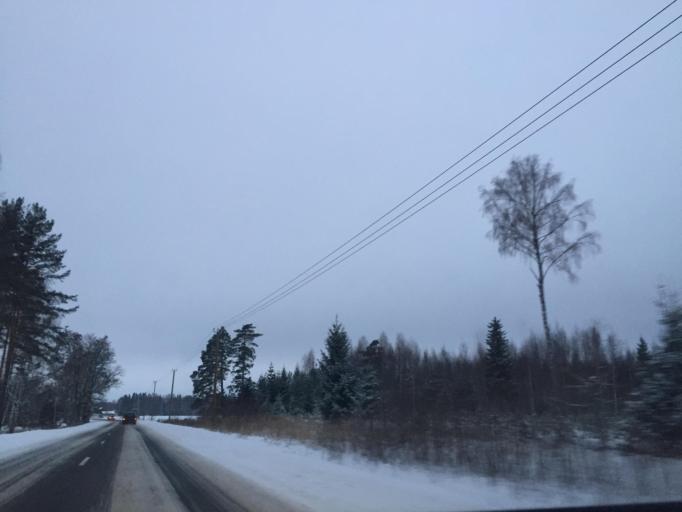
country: LV
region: Raunas
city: Rauna
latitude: 57.4356
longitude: 25.7122
